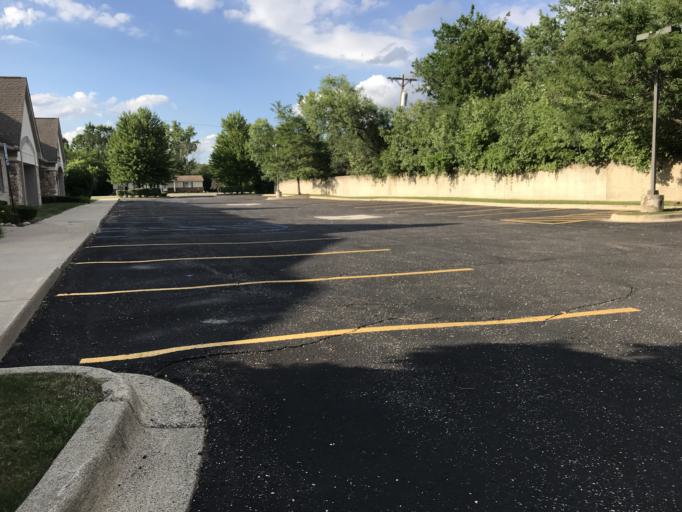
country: US
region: Michigan
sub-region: Oakland County
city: Farmington
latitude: 42.4693
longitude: -83.3514
